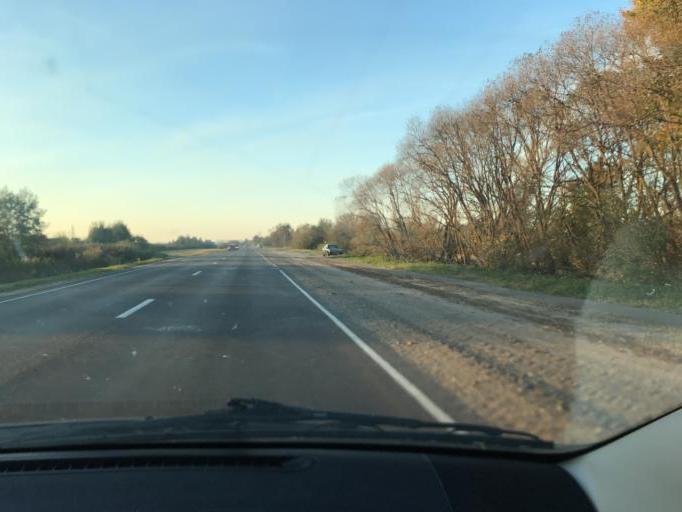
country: BY
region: Brest
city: Pinsk
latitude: 52.0853
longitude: 26.1358
